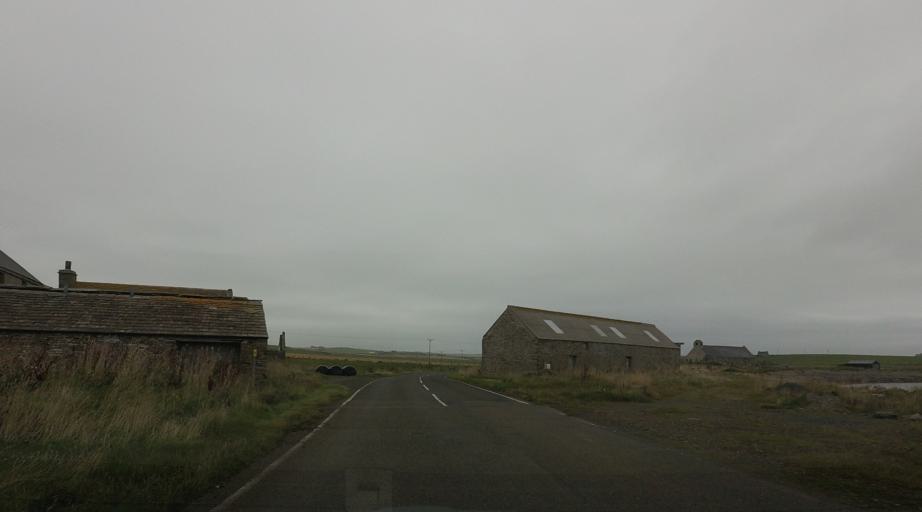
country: GB
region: Scotland
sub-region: Orkney Islands
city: Orkney
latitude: 58.7415
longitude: -2.9717
